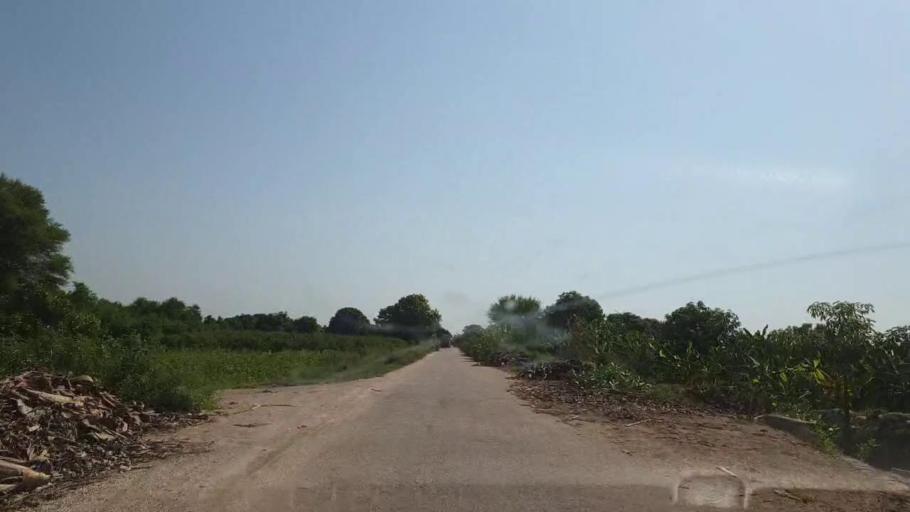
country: PK
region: Sindh
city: Tando Jam
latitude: 25.4168
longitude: 68.5821
